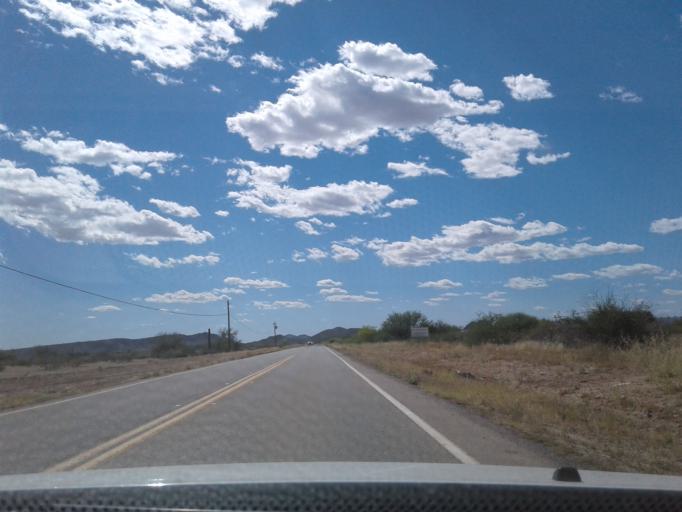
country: US
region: Arizona
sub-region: Maricopa County
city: Anthem
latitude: 33.7979
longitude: -112.2440
